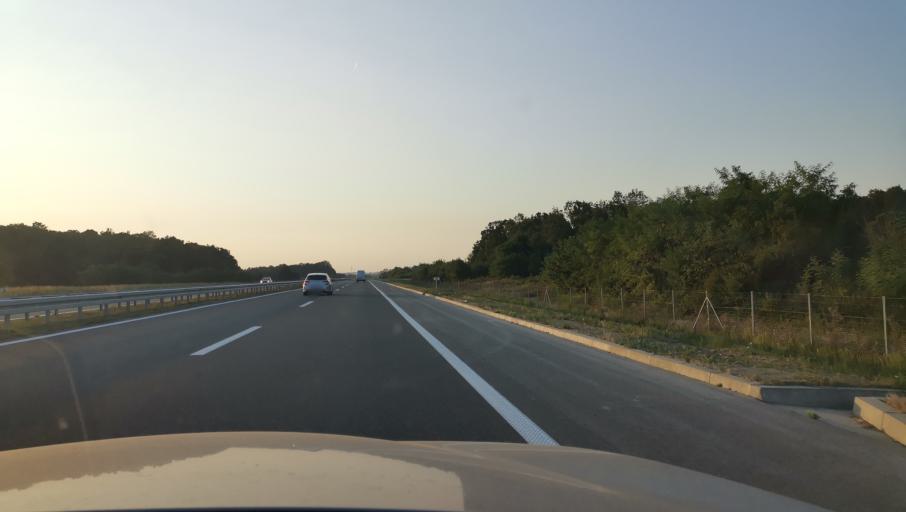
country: RS
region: Central Serbia
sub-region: Kolubarski Okrug
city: Lajkovac
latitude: 44.3862
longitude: 20.1087
